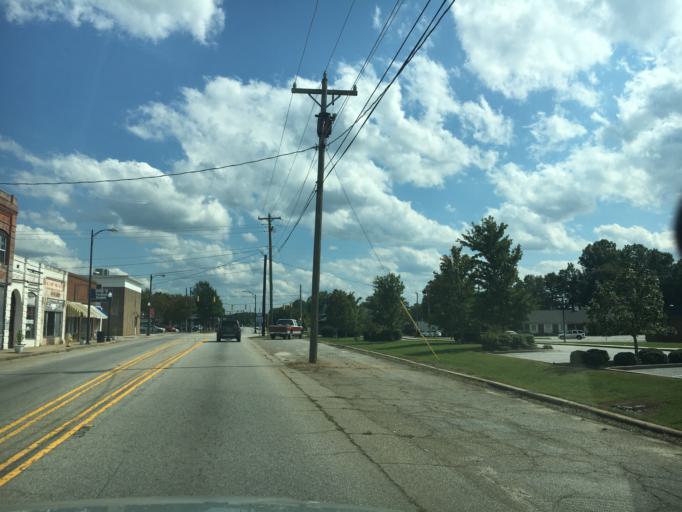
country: US
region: South Carolina
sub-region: Anderson County
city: Belton
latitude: 34.5240
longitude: -82.4948
